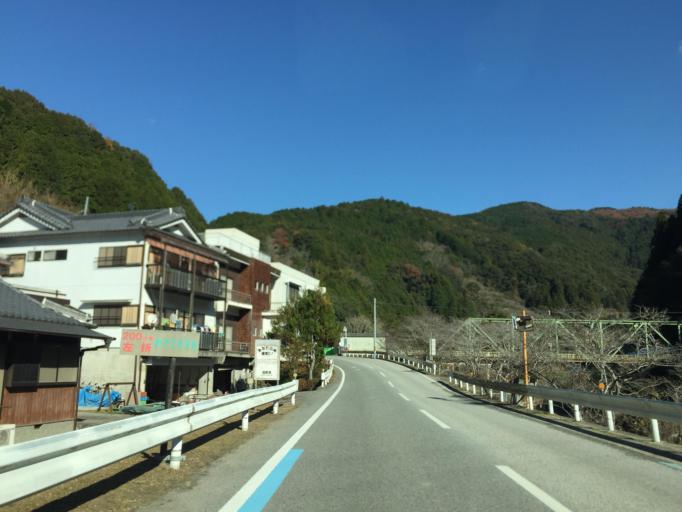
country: JP
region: Wakayama
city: Iwade
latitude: 34.1401
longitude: 135.4169
